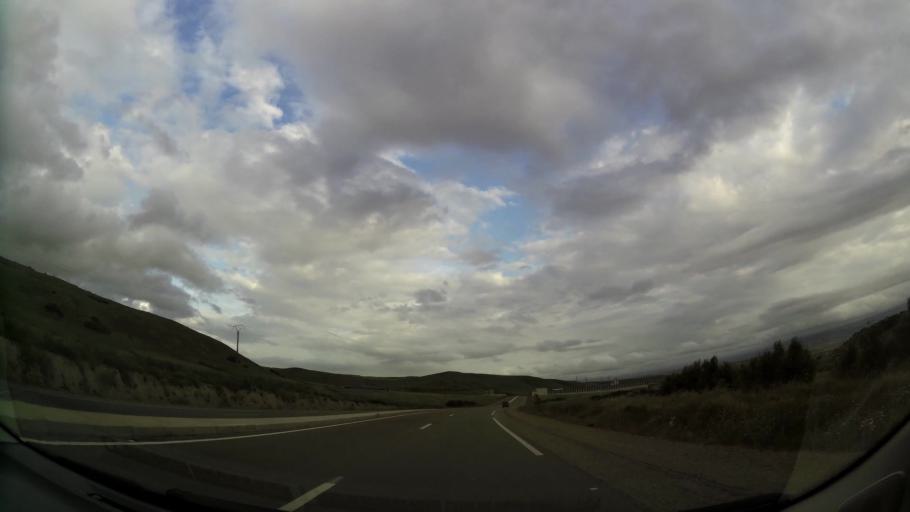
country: MA
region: Taza-Al Hoceima-Taounate
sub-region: Taza
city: Taza
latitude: 34.2854
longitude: -3.9598
